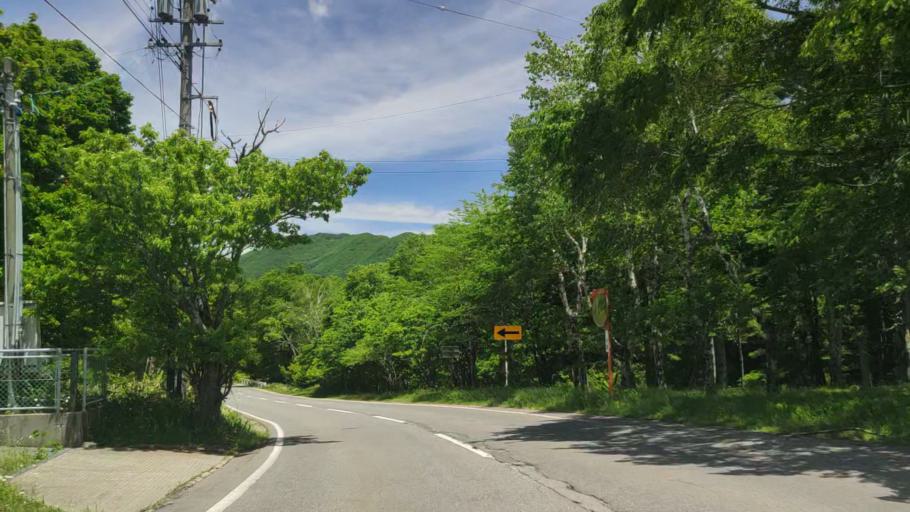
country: JP
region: Nagano
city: Suwa
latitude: 36.1288
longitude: 138.2293
